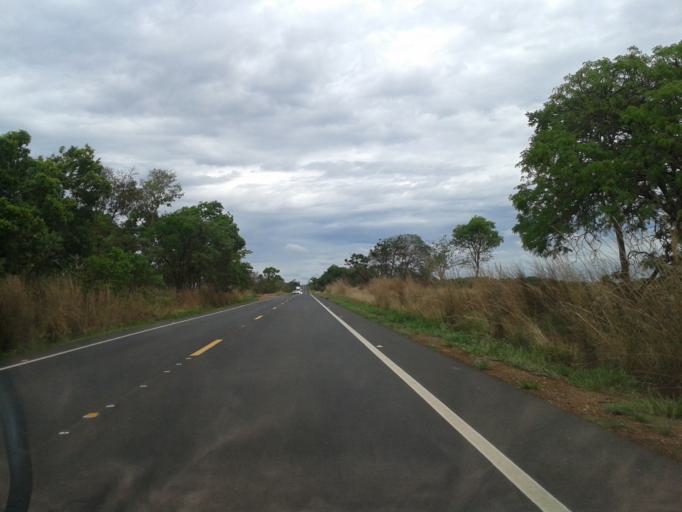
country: BR
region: Goias
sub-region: Caldas Novas
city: Caldas Novas
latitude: -17.8651
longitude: -48.6427
